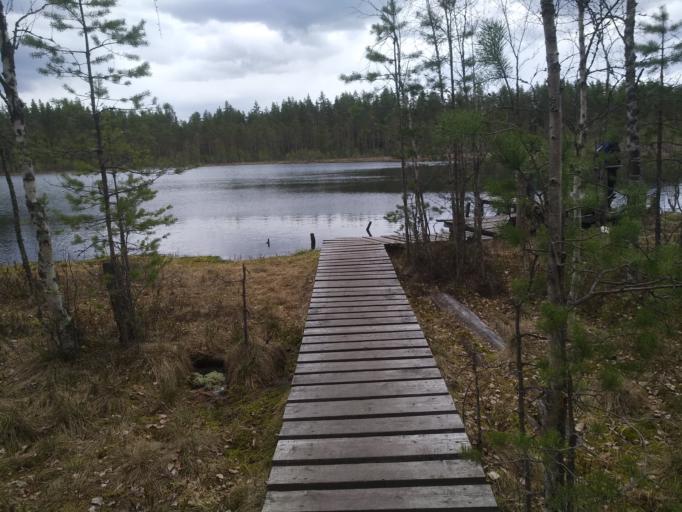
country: RU
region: Leningrad
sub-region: Vsevolzhskij Rajon
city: Vaskelovo
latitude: 60.5159
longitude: 30.4733
